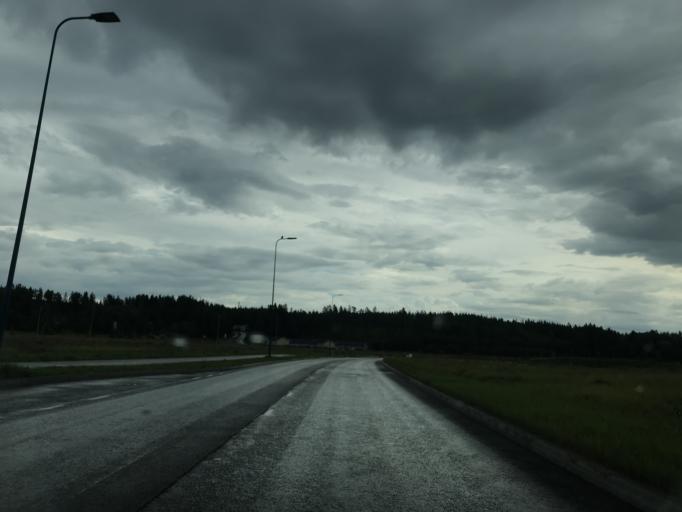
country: FI
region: Uusimaa
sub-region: Helsinki
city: Vihti
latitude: 60.3209
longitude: 24.3108
